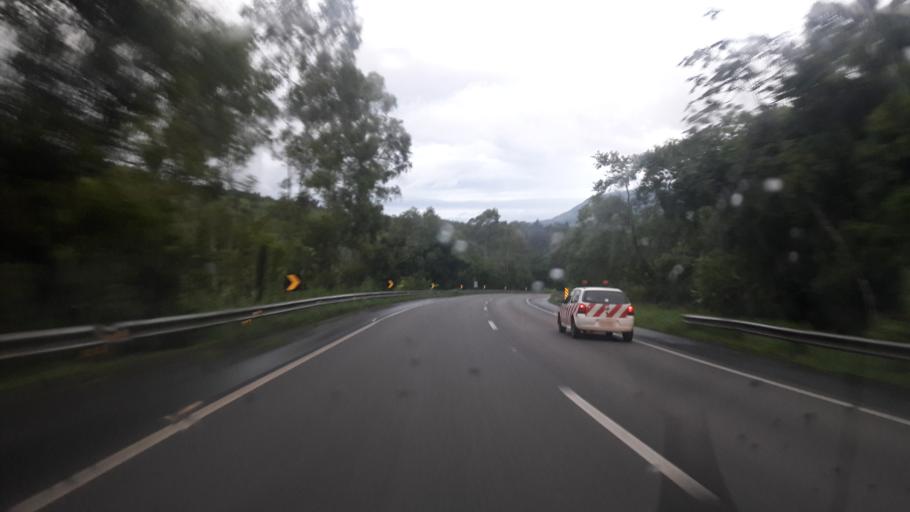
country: BR
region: Sao Paulo
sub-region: Cajati
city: Cajati
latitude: -24.7788
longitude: -48.2002
